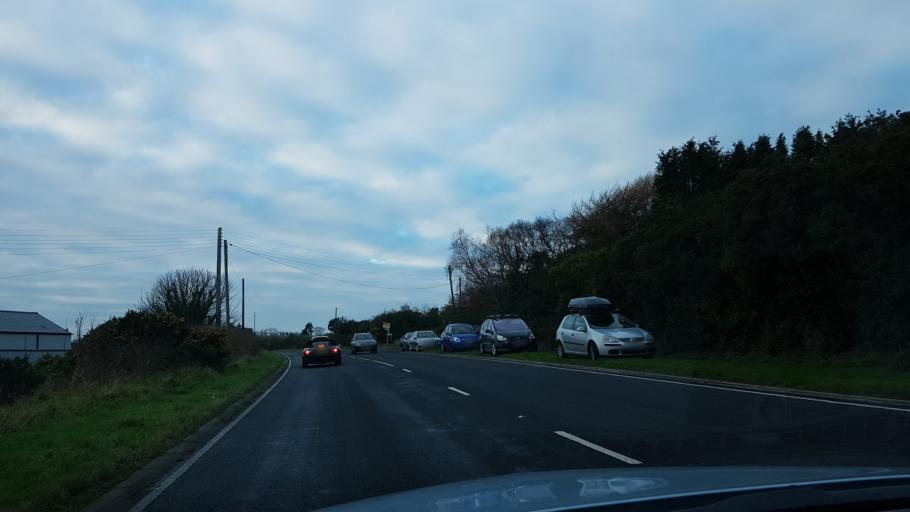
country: GB
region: Northern Ireland
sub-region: Down District
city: Donaghadee
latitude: 54.6705
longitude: -5.5787
